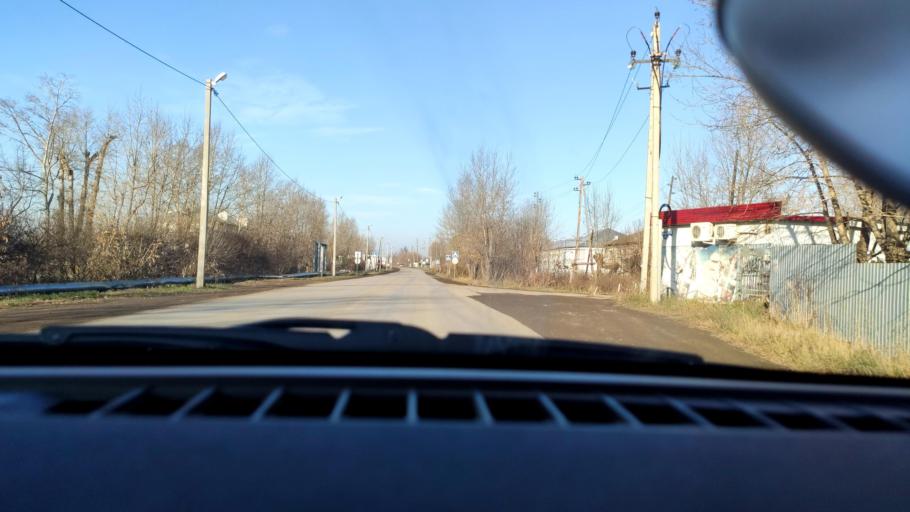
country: RU
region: Perm
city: Kondratovo
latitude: 57.9806
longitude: 56.1063
